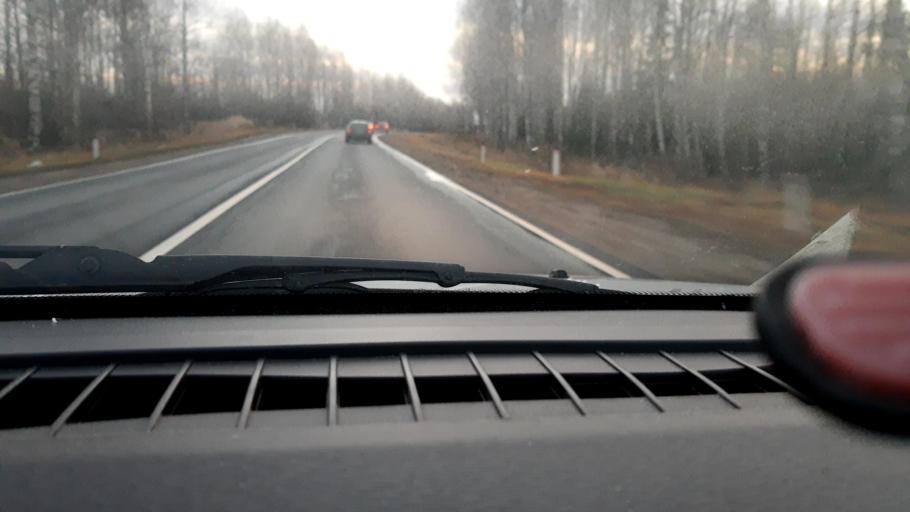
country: RU
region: Nizjnij Novgorod
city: Krasnyye Baki
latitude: 57.0749
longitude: 45.1431
